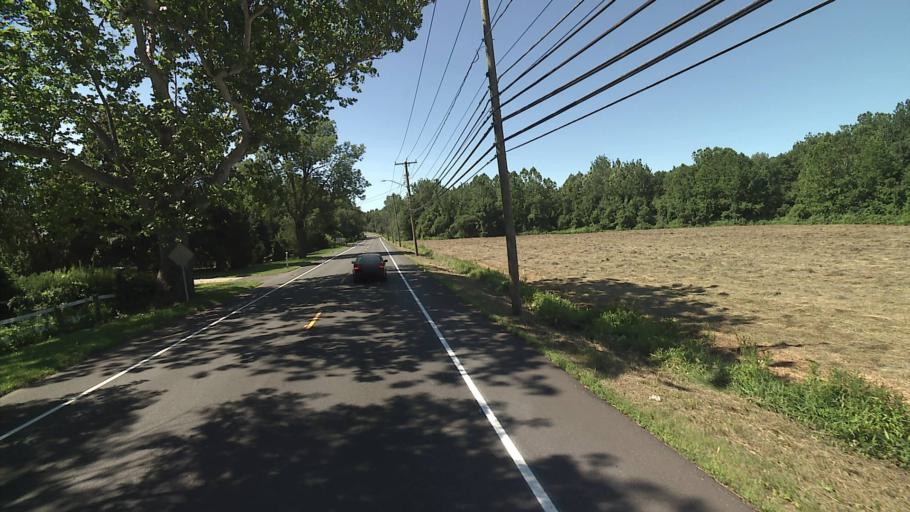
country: US
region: Connecticut
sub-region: Hartford County
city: Salmon Brook
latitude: 41.9436
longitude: -72.7919
